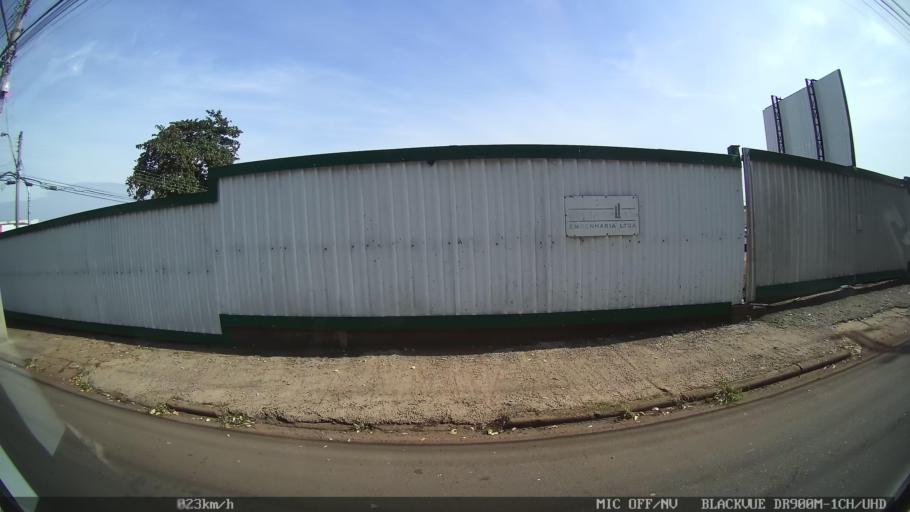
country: BR
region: Sao Paulo
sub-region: Piracicaba
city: Piracicaba
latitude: -22.7131
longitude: -47.6567
